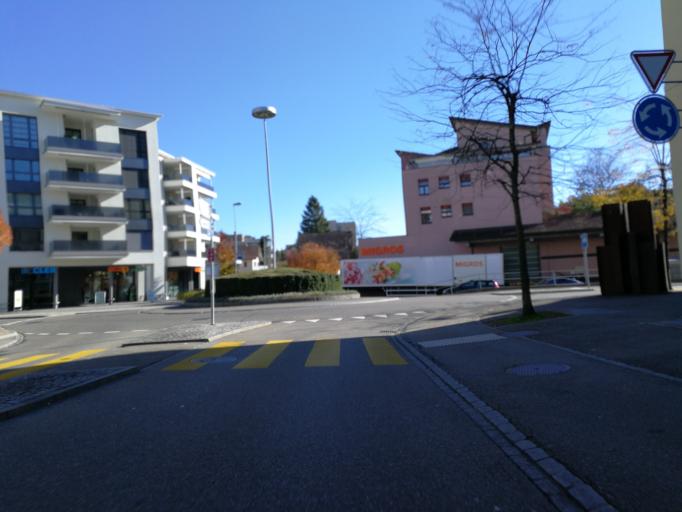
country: CH
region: Saint Gallen
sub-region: Wahlkreis See-Gaster
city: Jona
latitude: 47.2319
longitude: 8.8364
